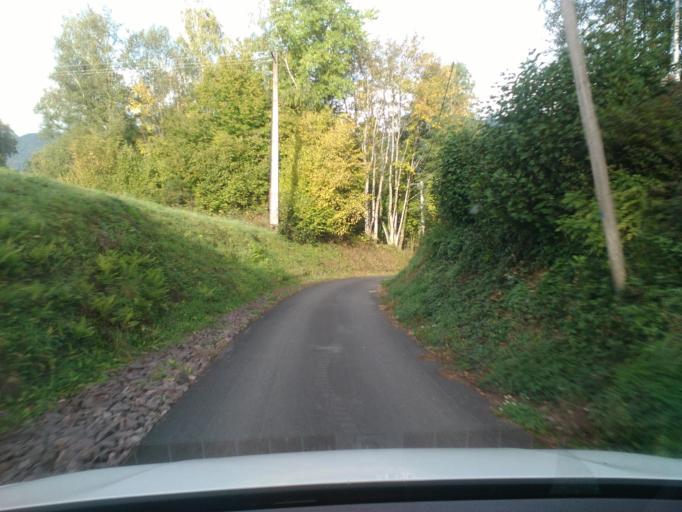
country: FR
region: Lorraine
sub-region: Departement des Vosges
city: Senones
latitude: 48.3937
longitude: 7.0045
